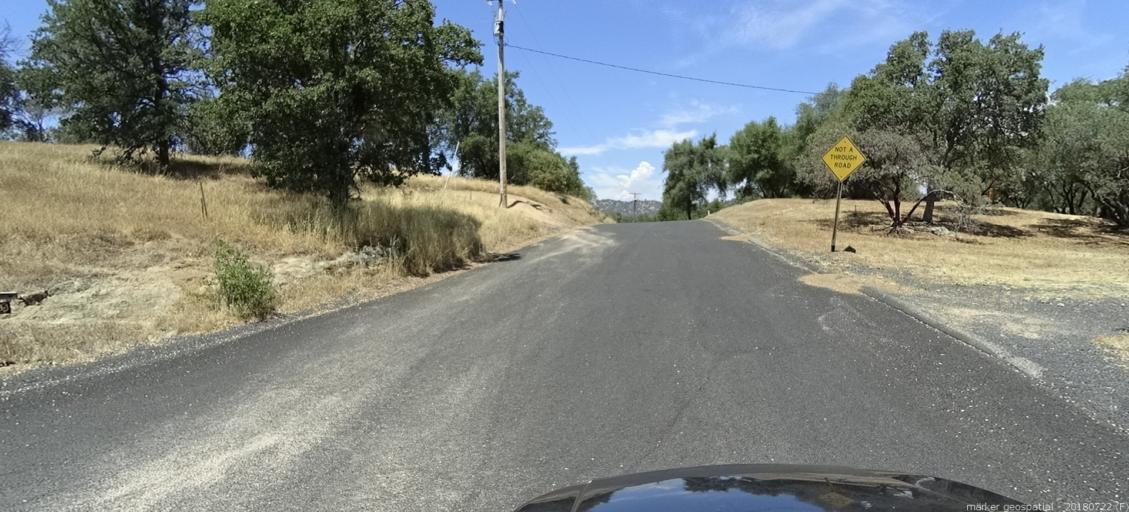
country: US
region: California
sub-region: Madera County
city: Yosemite Lakes
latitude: 37.2134
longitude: -119.7342
